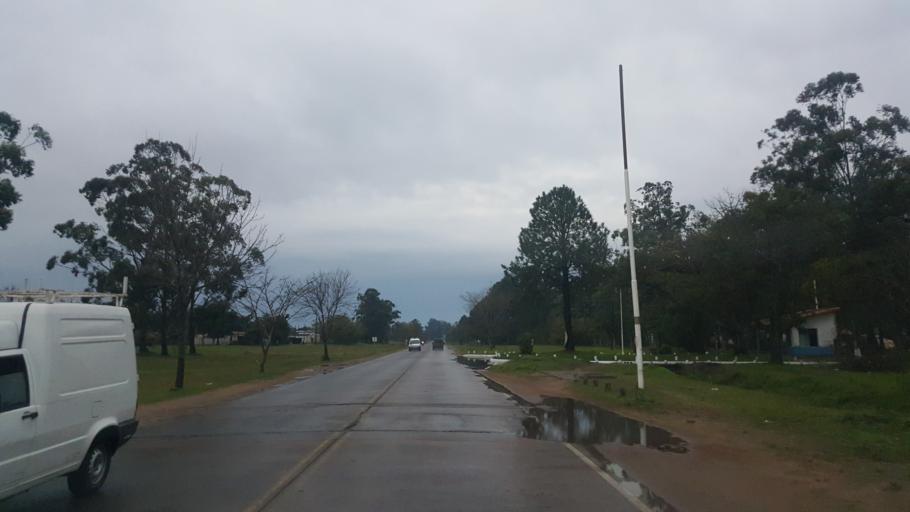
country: AR
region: Corrientes
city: Ituzaingo
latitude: -27.5877
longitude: -56.6824
